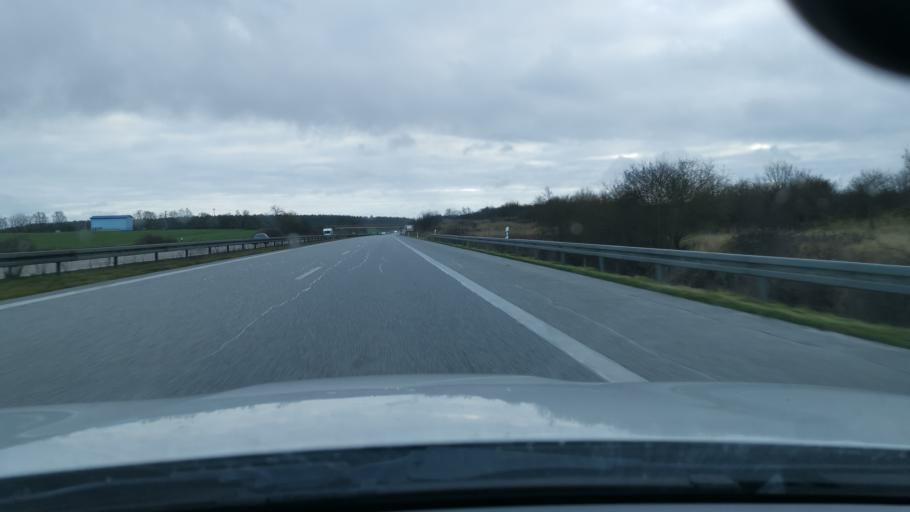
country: DE
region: Mecklenburg-Vorpommern
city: Krakow am See
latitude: 53.6400
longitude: 12.3713
